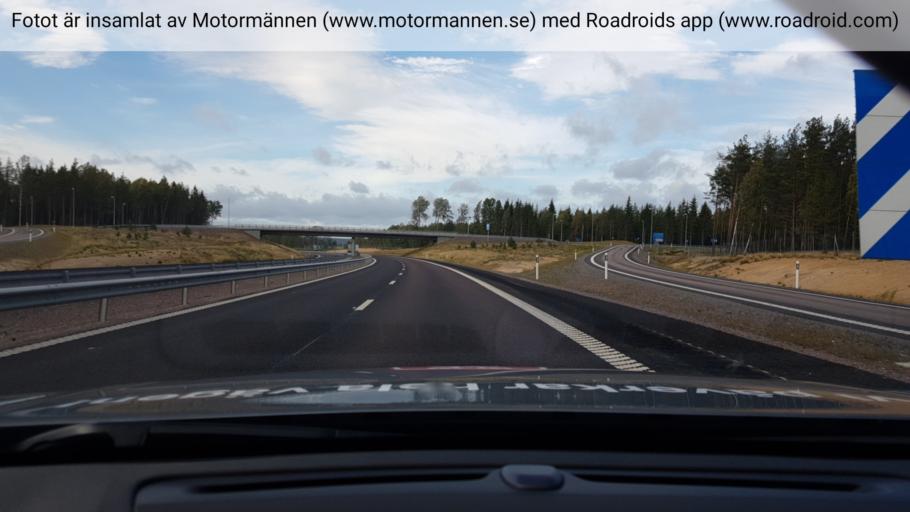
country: SE
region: Vaermland
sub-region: Karlstads Kommun
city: Edsvalla
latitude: 59.3921
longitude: 13.2879
